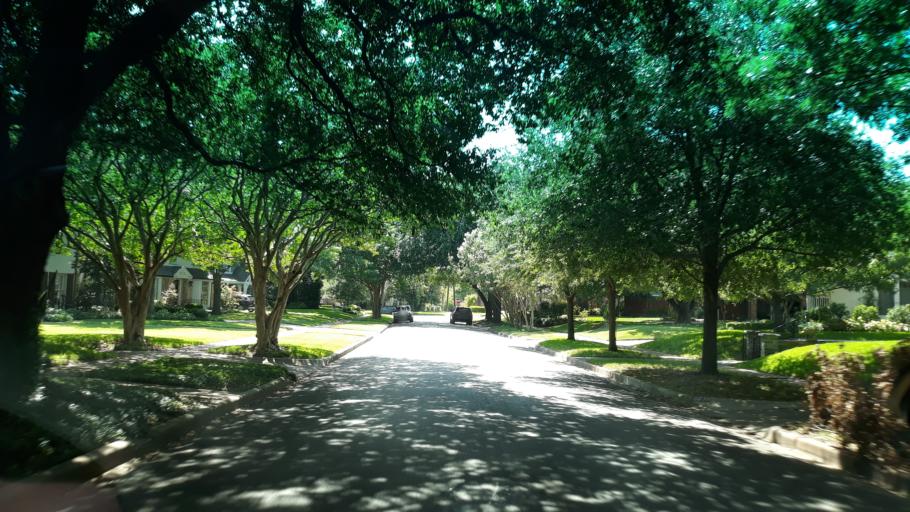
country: US
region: Texas
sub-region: Dallas County
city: Highland Park
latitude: 32.8176
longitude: -96.7488
